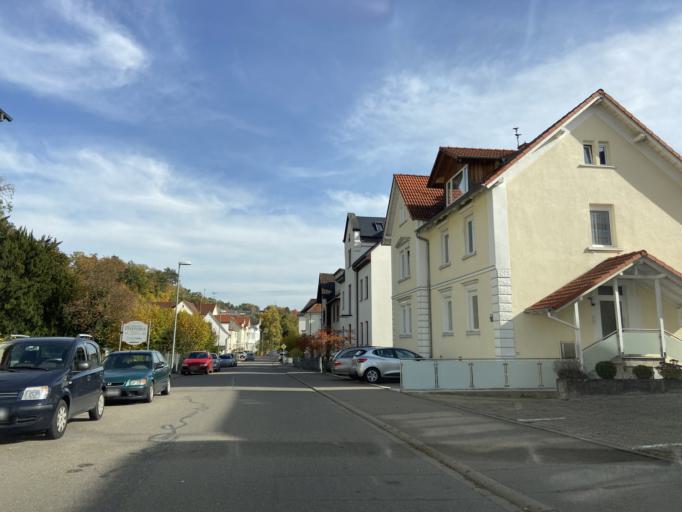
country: DE
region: Baden-Wuerttemberg
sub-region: Tuebingen Region
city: Sigmaringen
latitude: 48.0914
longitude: 9.2092
